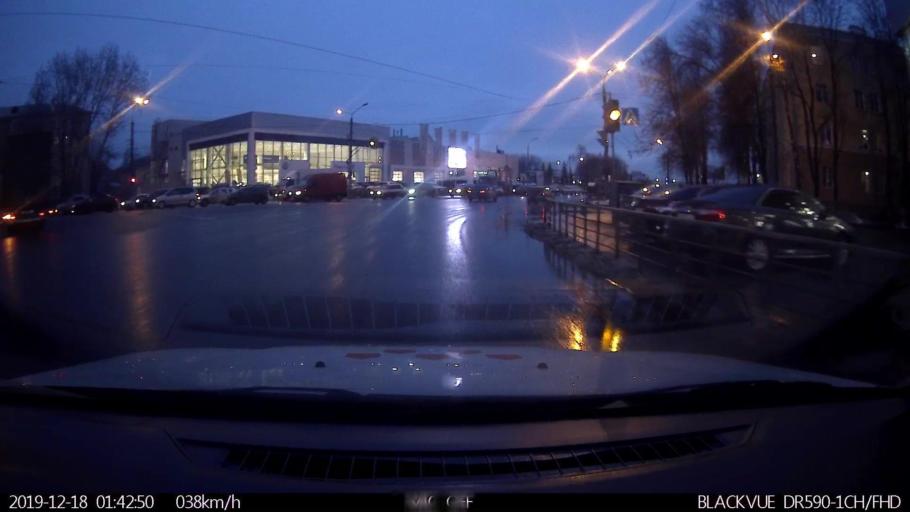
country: RU
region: Nizjnij Novgorod
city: Nizhniy Novgorod
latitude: 56.3137
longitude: 43.8975
